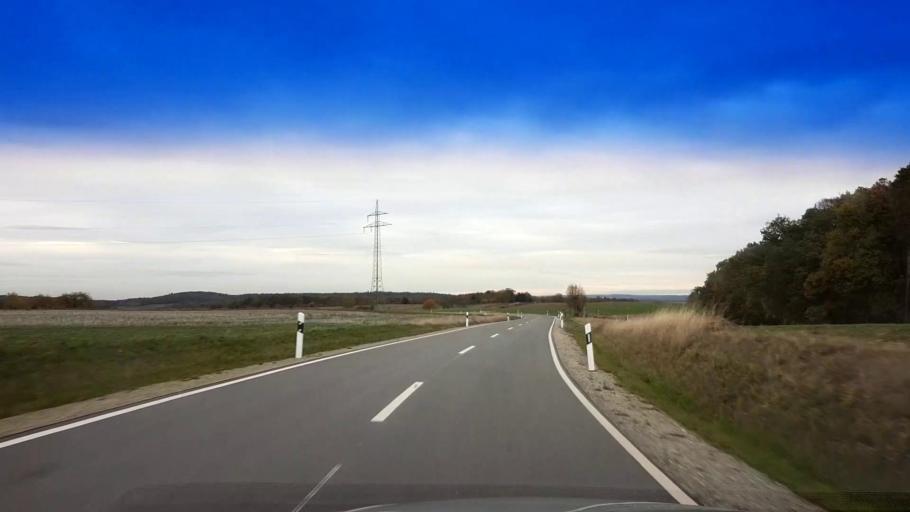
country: DE
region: Bavaria
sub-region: Upper Franconia
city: Priesendorf
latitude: 49.9260
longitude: 10.7066
